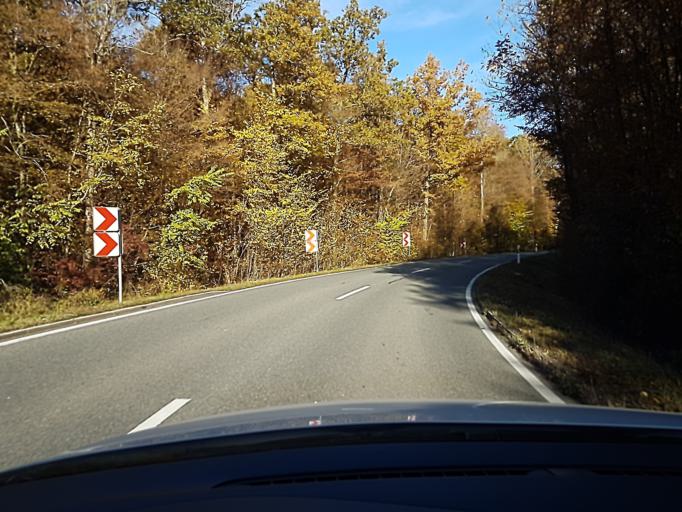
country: DE
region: Baden-Wuerttemberg
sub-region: Karlsruhe Region
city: Fahrenbach
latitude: 49.3986
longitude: 9.1844
